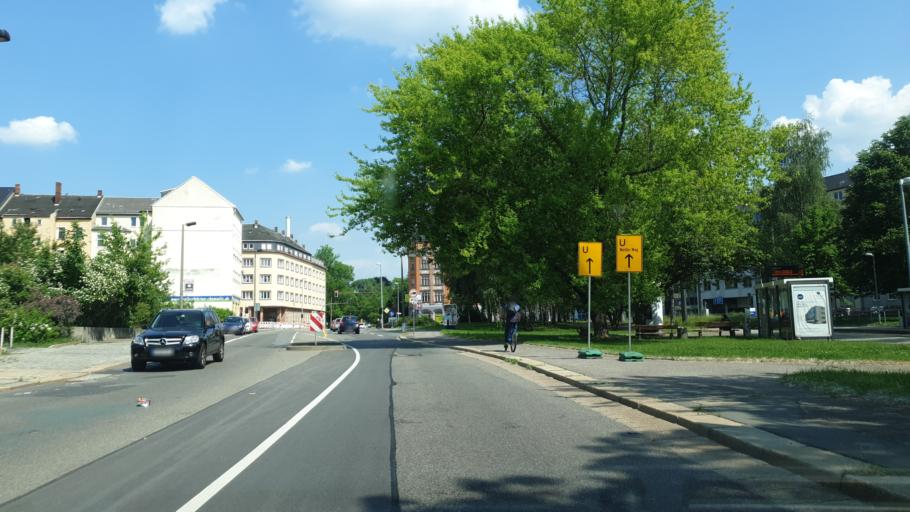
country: DE
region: Saxony
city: Chemnitz
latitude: 50.8309
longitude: 12.9373
